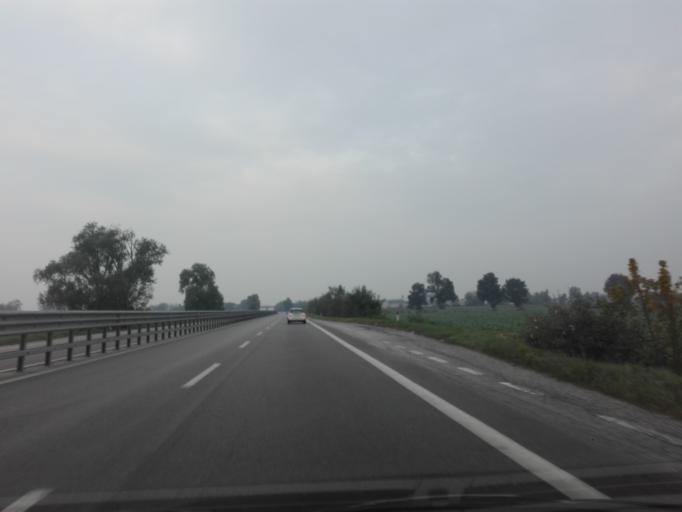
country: IT
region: Veneto
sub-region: Provincia di Rovigo
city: Fratta Polesine
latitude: 45.0227
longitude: 11.6316
